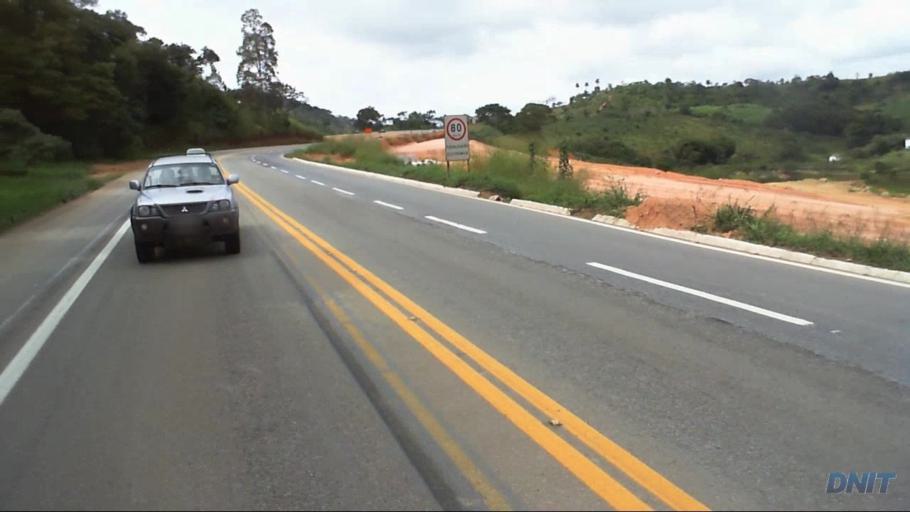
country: BR
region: Minas Gerais
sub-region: Caete
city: Caete
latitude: -19.7468
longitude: -43.6224
